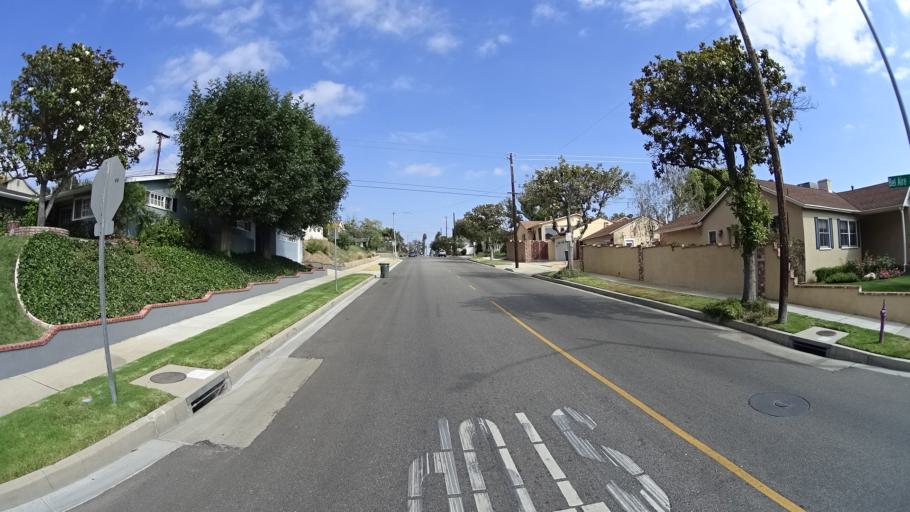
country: US
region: California
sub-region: Los Angeles County
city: Burbank
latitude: 34.1989
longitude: -118.3108
